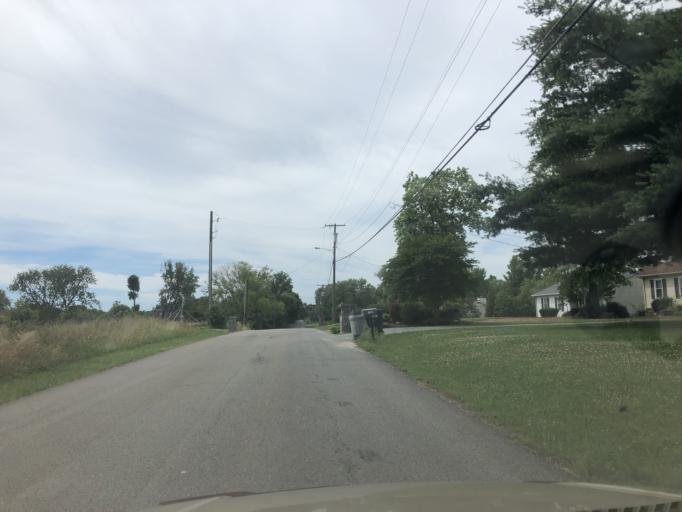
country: US
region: Tennessee
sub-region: Davidson County
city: Lakewood
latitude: 36.2562
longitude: -86.6152
